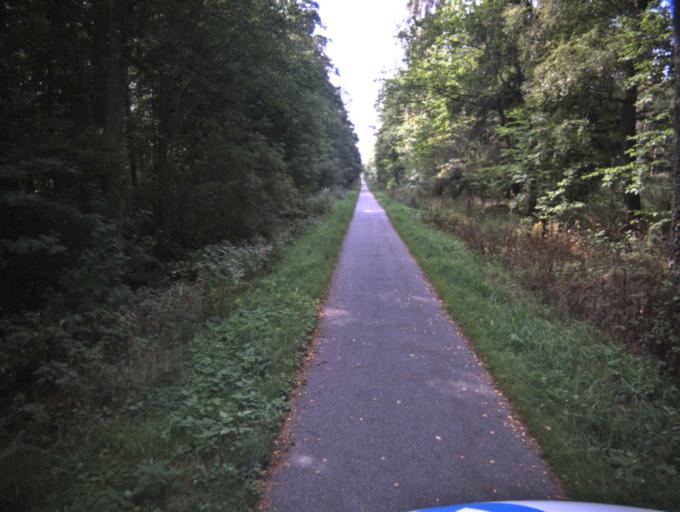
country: SE
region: Vaestra Goetaland
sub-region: Ulricehamns Kommun
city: Ulricehamn
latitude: 57.6674
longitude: 13.3668
